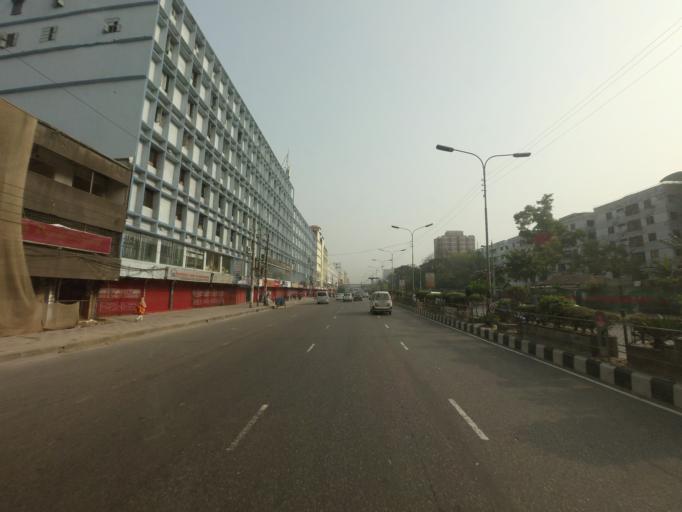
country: BD
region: Dhaka
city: Paltan
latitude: 23.7861
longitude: 90.3995
